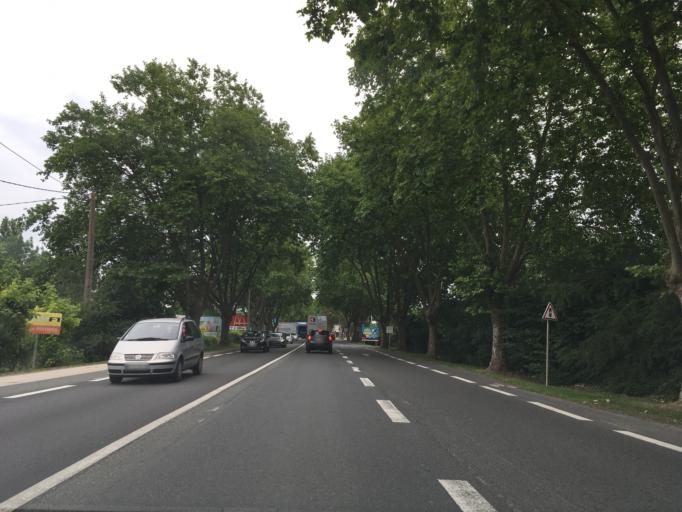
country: FR
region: Poitou-Charentes
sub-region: Departement des Deux-Sevres
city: Niort
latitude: 46.3084
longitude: -0.4838
